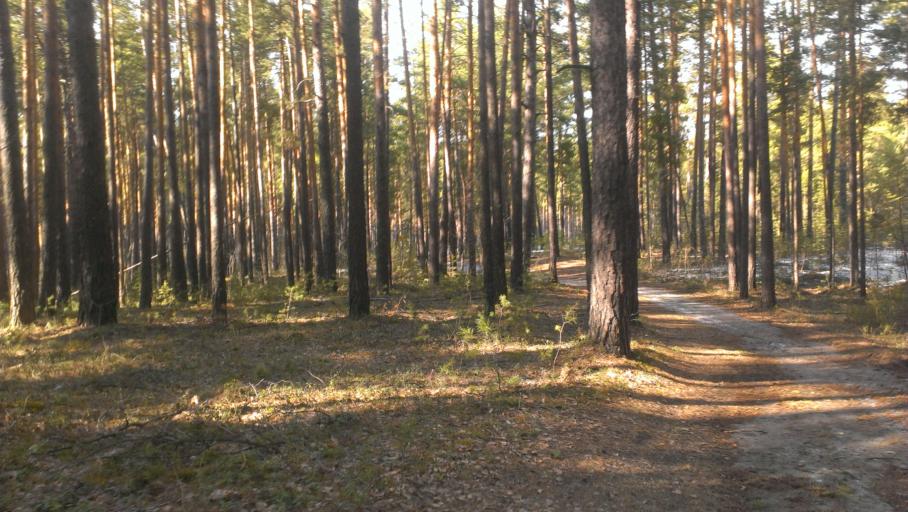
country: RU
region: Altai Krai
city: Yuzhnyy
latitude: 53.2831
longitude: 83.6994
